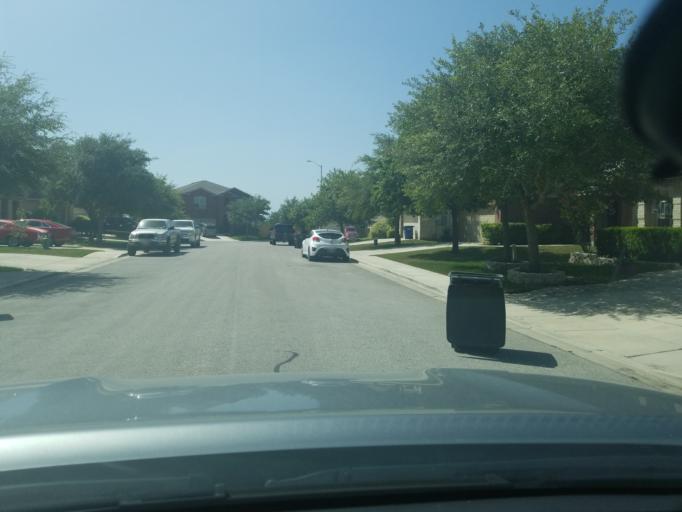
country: US
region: Texas
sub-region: Guadalupe County
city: Lake Dunlap
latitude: 29.6712
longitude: -98.0408
